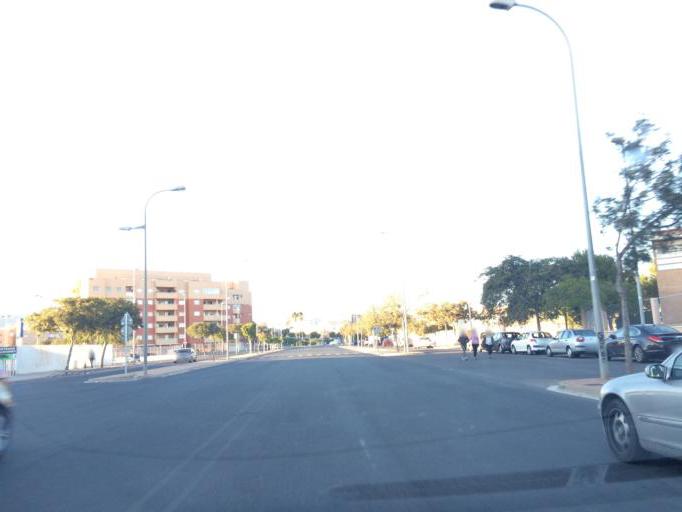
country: ES
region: Andalusia
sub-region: Provincia de Almeria
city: Almeria
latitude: 36.8451
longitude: -2.4333
